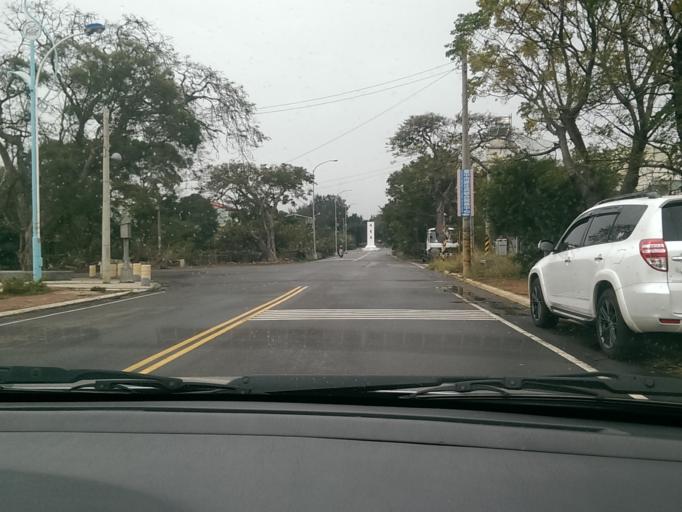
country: TW
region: Taiwan
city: Fengyuan
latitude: 24.2366
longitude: 120.6206
